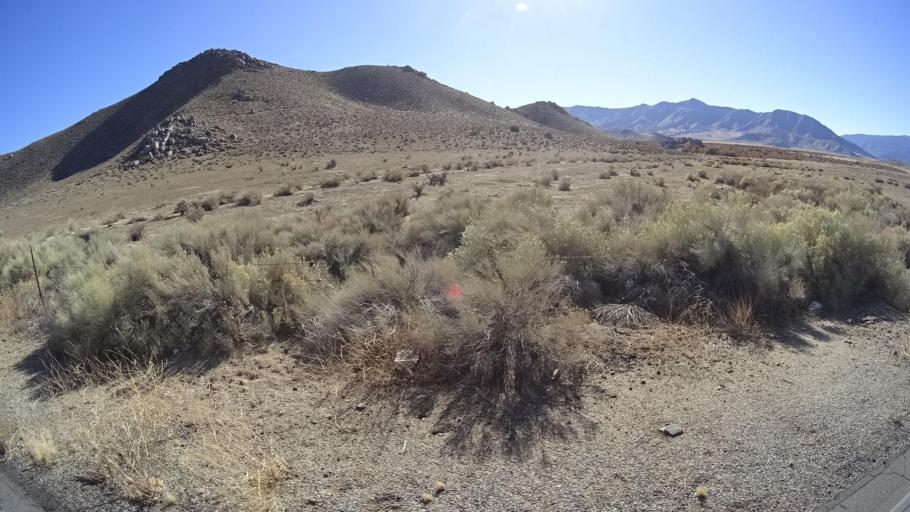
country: US
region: California
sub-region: Kern County
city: Weldon
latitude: 35.6797
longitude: -118.3646
